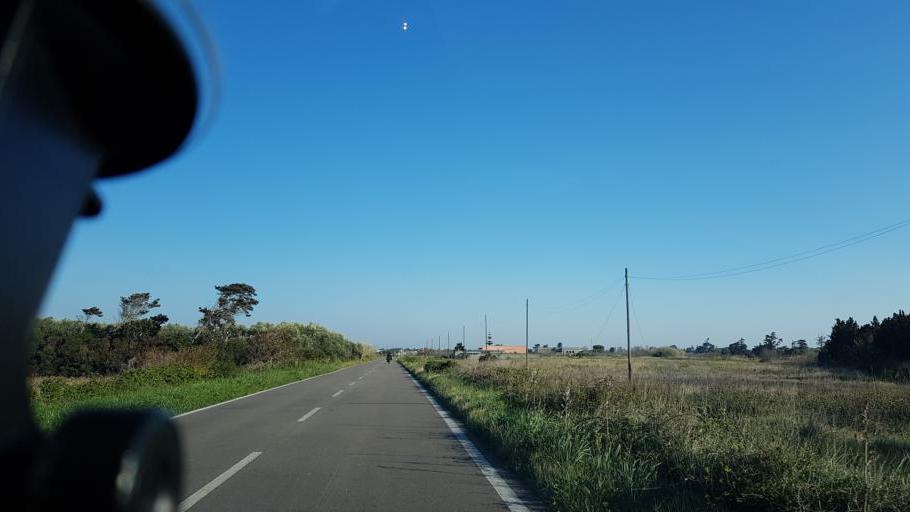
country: IT
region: Apulia
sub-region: Provincia di Lecce
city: Giorgilorio
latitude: 40.4395
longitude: 18.2359
